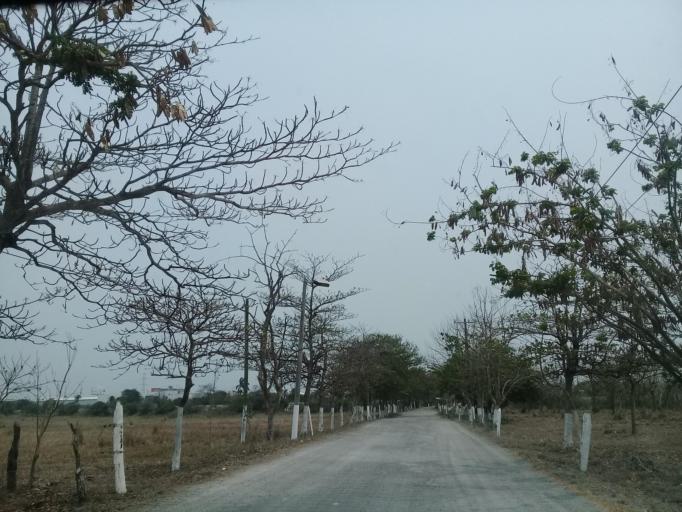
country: MX
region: Veracruz
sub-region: Veracruz
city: Las Amapolas
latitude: 19.1656
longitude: -96.2087
